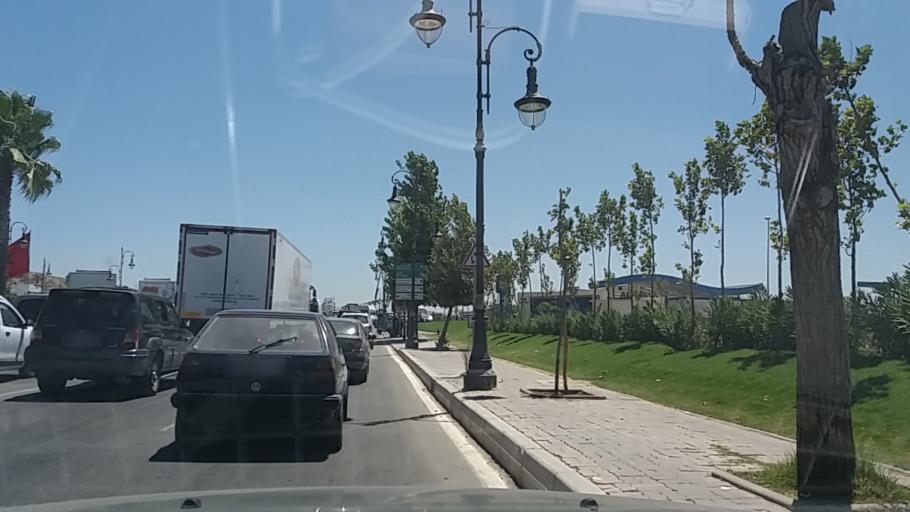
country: MA
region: Tanger-Tetouan
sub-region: Tanger-Assilah
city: Tangier
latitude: 35.7540
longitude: -5.7904
